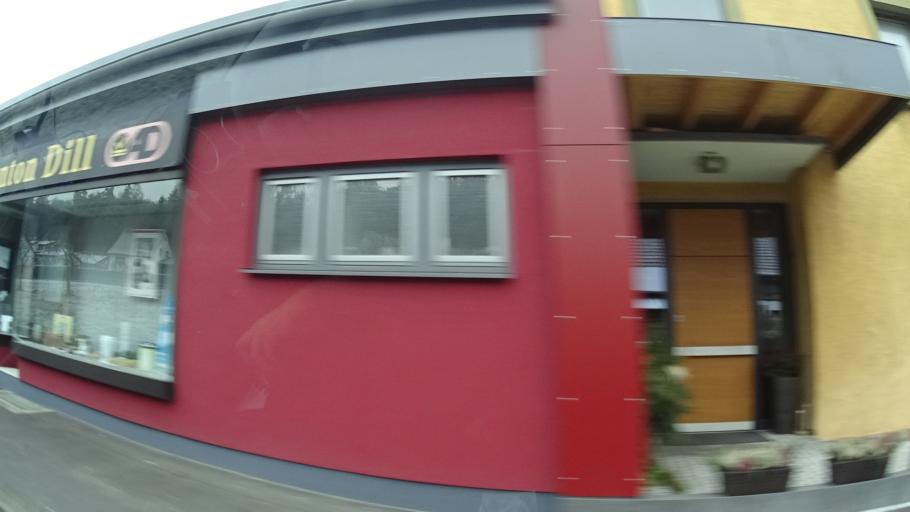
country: DE
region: Bavaria
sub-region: Regierungsbezirk Unterfranken
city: Bad Bruckenau
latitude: 50.2879
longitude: 9.7349
